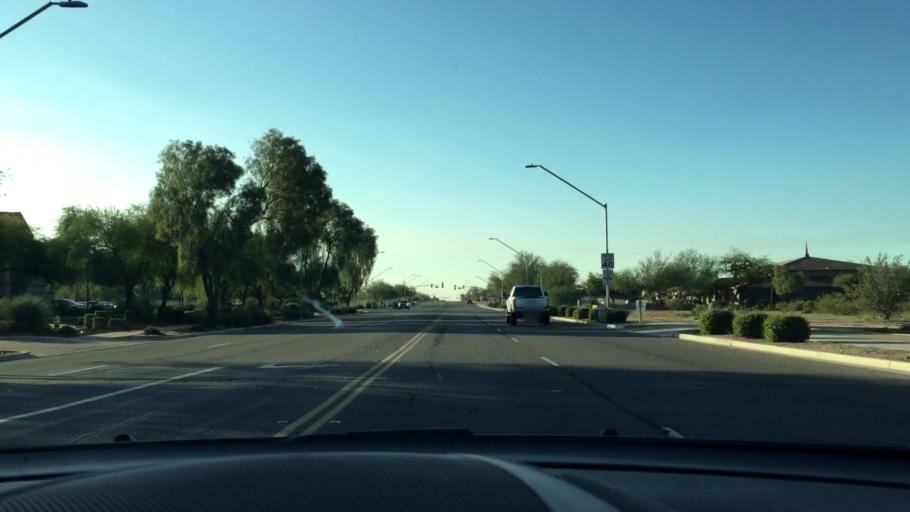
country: US
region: Arizona
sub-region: Maricopa County
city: Sun City
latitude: 33.6956
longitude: -112.2031
